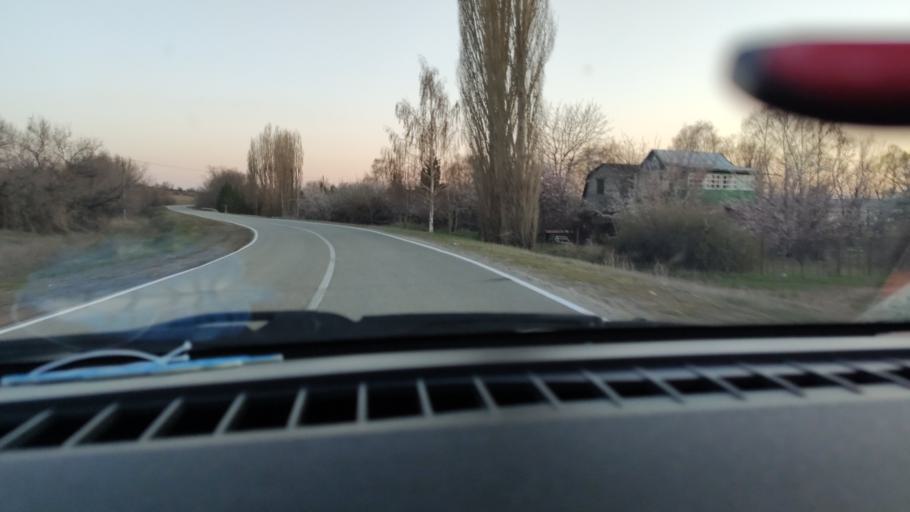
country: RU
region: Saratov
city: Privolzhskiy
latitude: 51.2194
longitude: 45.9190
